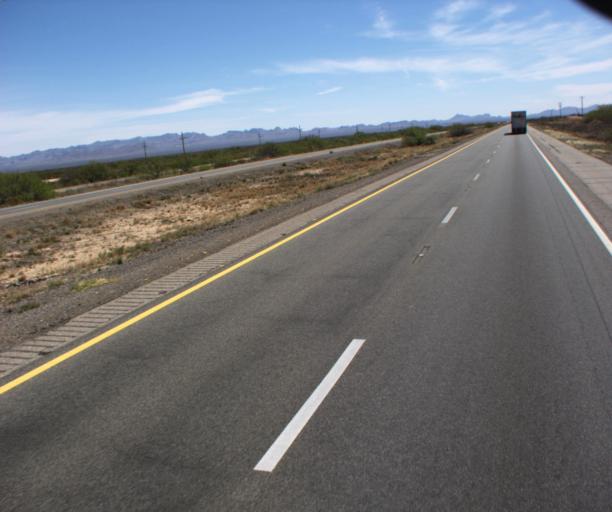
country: US
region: Arizona
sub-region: Cochise County
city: Willcox
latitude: 32.2929
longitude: -109.3355
